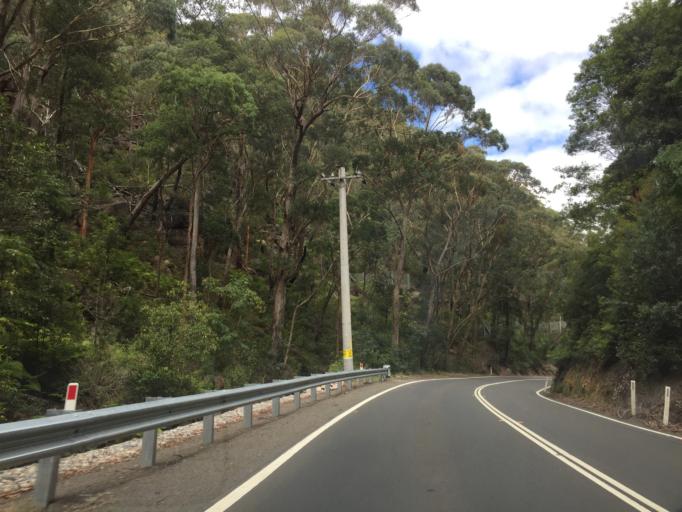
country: AU
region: New South Wales
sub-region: Hawkesbury
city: Richmond
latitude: -33.5185
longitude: 150.6228
